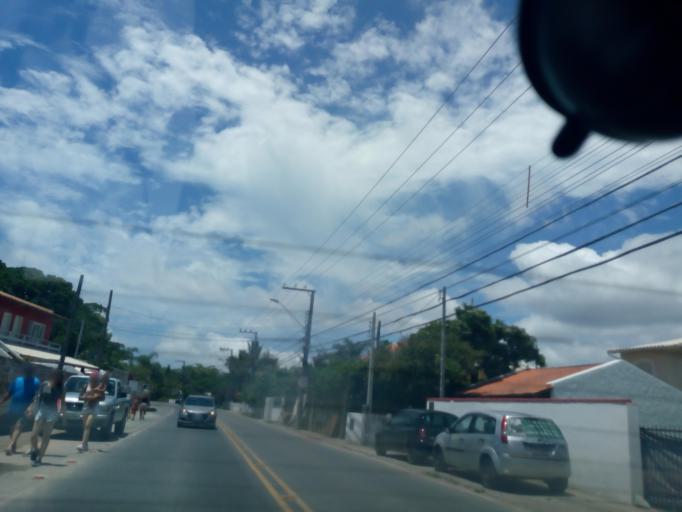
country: BR
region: Santa Catarina
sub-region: Florianopolis
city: Itacorubi
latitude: -27.4041
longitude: -48.4267
